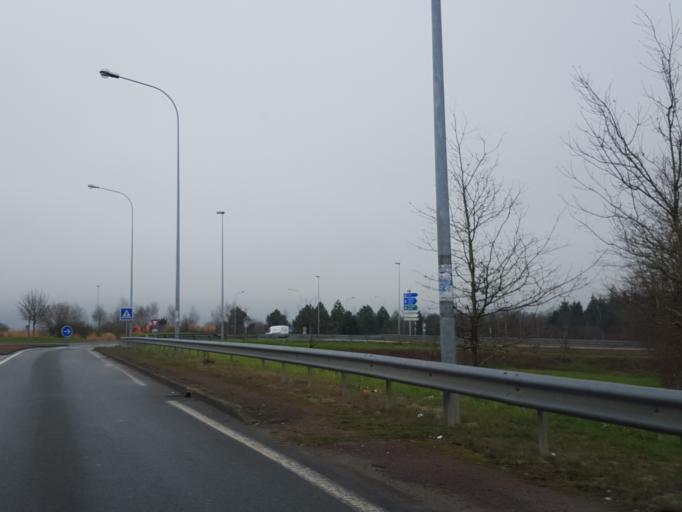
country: FR
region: Pays de la Loire
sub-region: Departement de la Vendee
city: La Roche-sur-Yon
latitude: 46.6767
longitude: -1.3987
